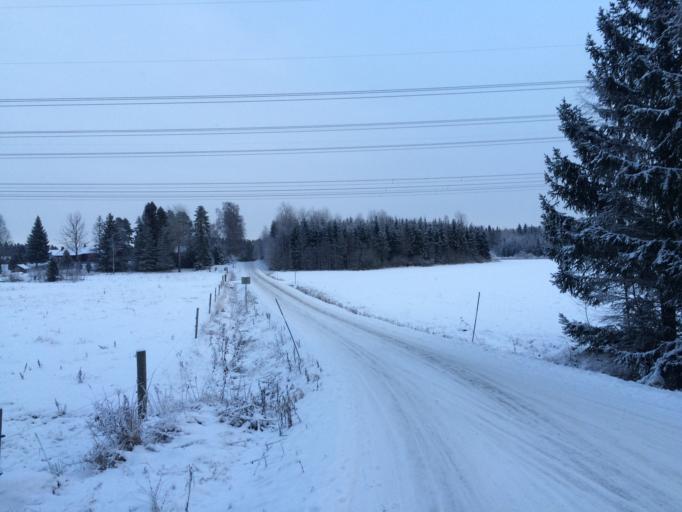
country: SE
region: Uppsala
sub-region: Enkopings Kommun
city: Orsundsbro
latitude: 59.9083
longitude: 17.1860
